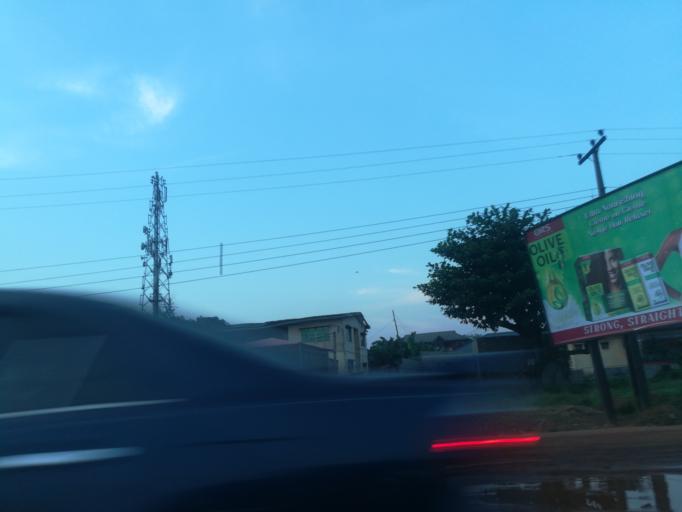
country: NG
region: Ogun
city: Abeokuta
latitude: 7.1780
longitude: 3.3940
